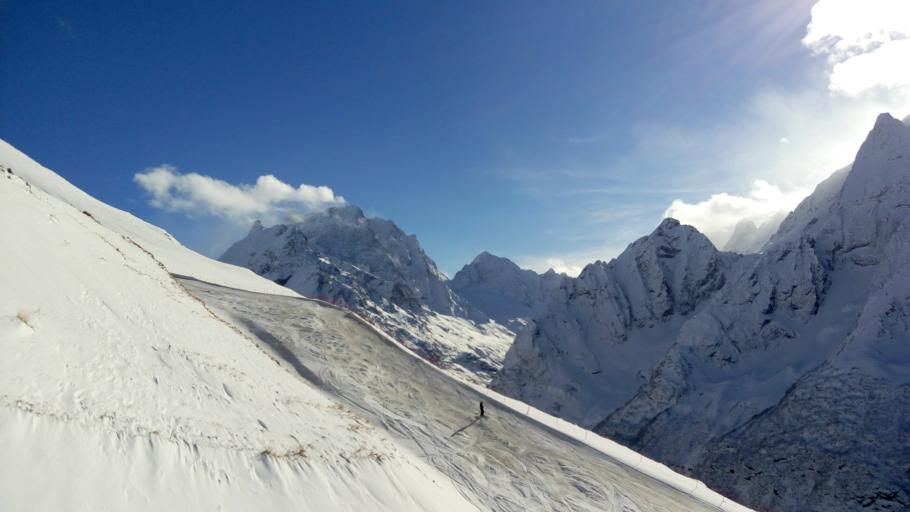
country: RU
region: Karachayevo-Cherkesiya
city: Teberda
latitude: 43.2913
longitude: 41.6582
